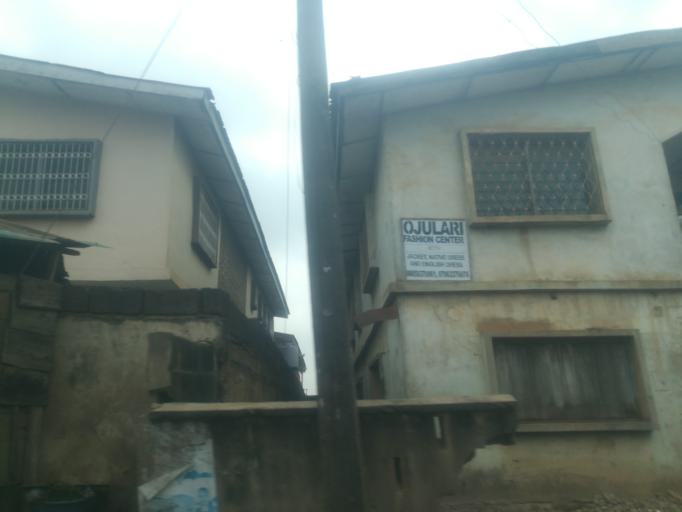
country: NG
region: Oyo
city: Ibadan
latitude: 7.4016
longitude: 3.9366
